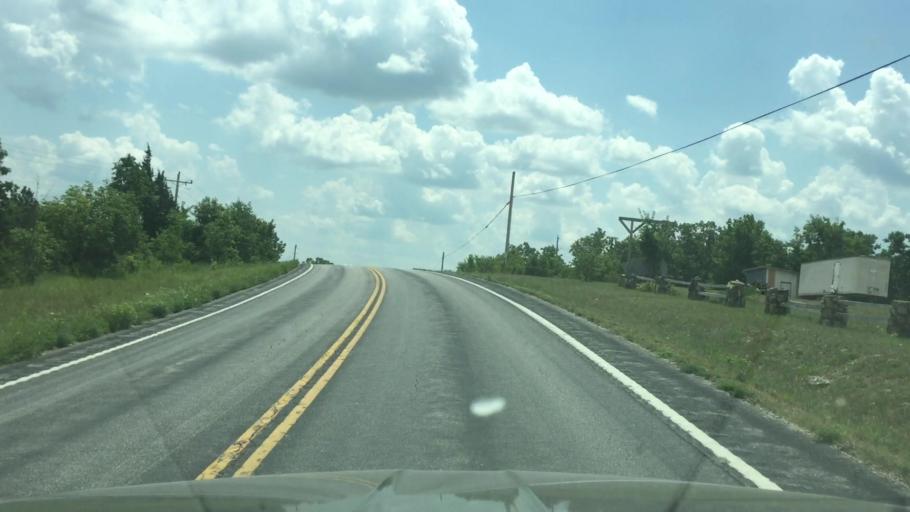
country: US
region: Missouri
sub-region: Miller County
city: Tuscumbia
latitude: 38.1060
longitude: -92.5007
